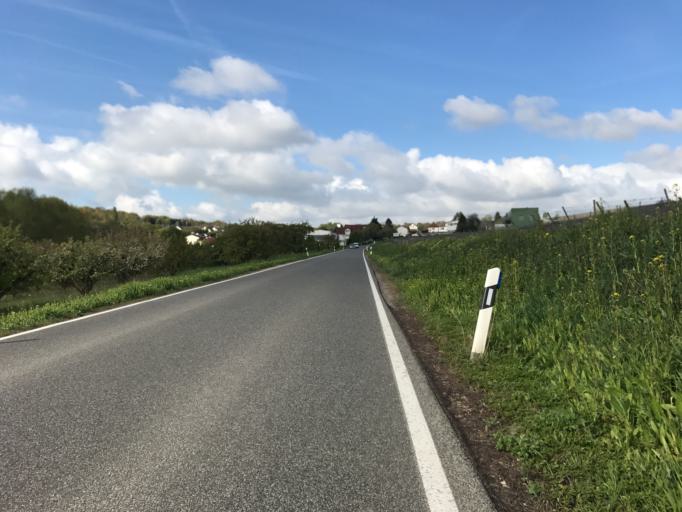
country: DE
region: Rheinland-Pfalz
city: Engelstadt
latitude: 49.9072
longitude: 8.0742
